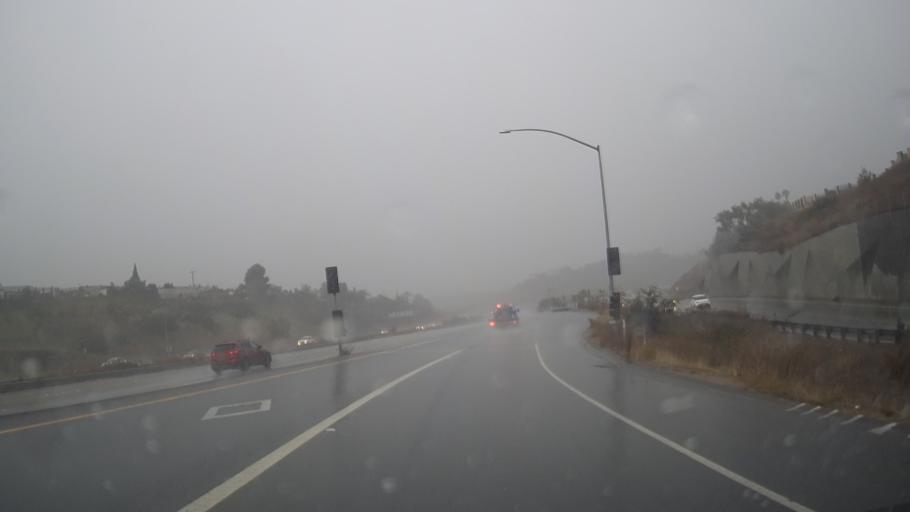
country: US
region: California
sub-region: San Diego County
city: Bonita
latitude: 32.6645
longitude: -117.0587
